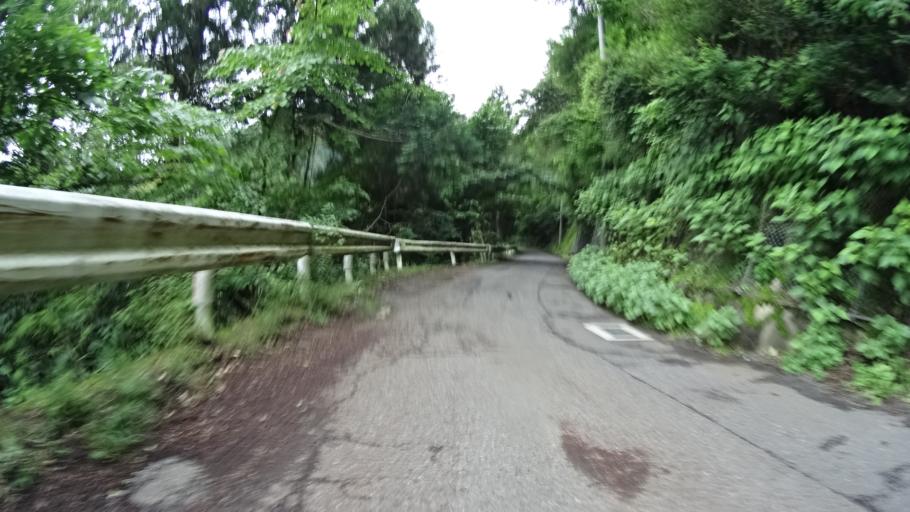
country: JP
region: Kanagawa
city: Hadano
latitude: 35.4748
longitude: 139.2110
